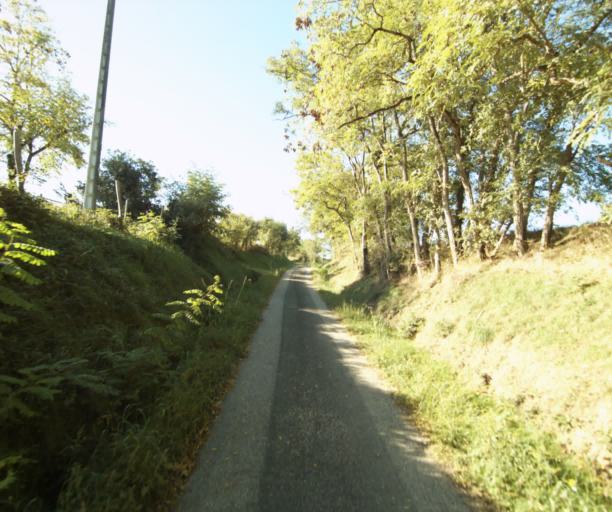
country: FR
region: Midi-Pyrenees
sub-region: Departement du Gers
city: Gondrin
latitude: 43.8443
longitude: 0.2235
